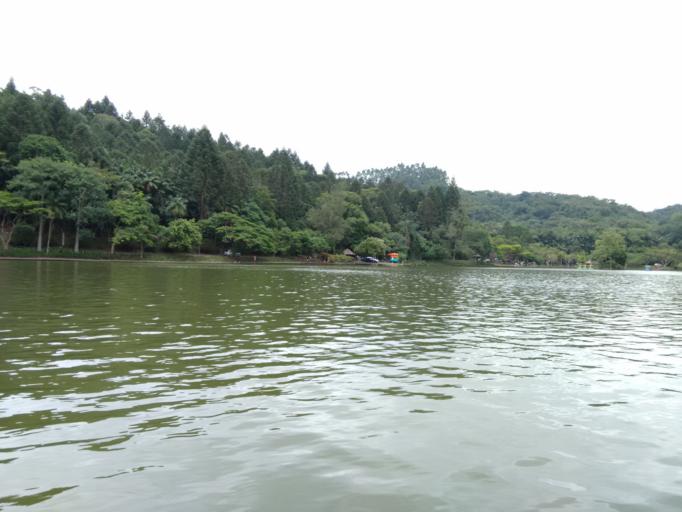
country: BR
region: Santa Catarina
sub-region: Jaragua Do Sul
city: Jaragua do Sul
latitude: -26.5060
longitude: -49.1284
